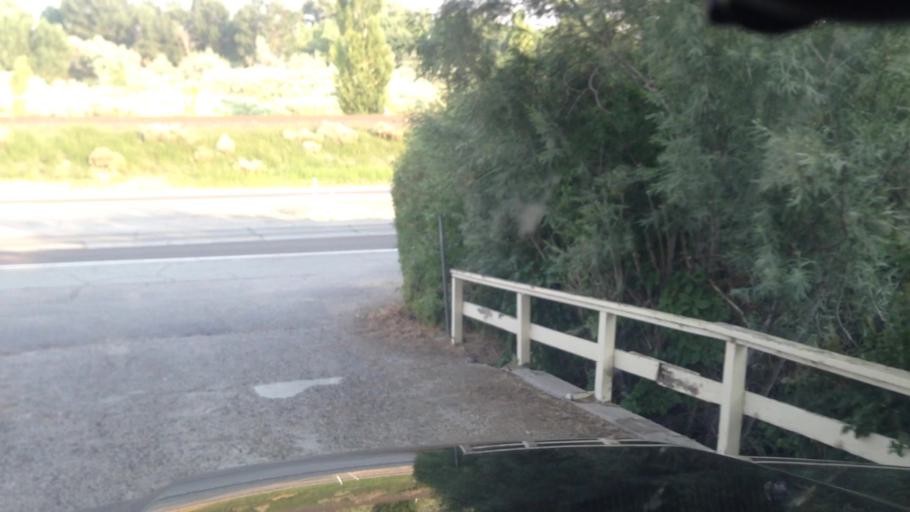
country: US
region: Nevada
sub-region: Washoe County
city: Reno
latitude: 39.5189
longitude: -119.8492
